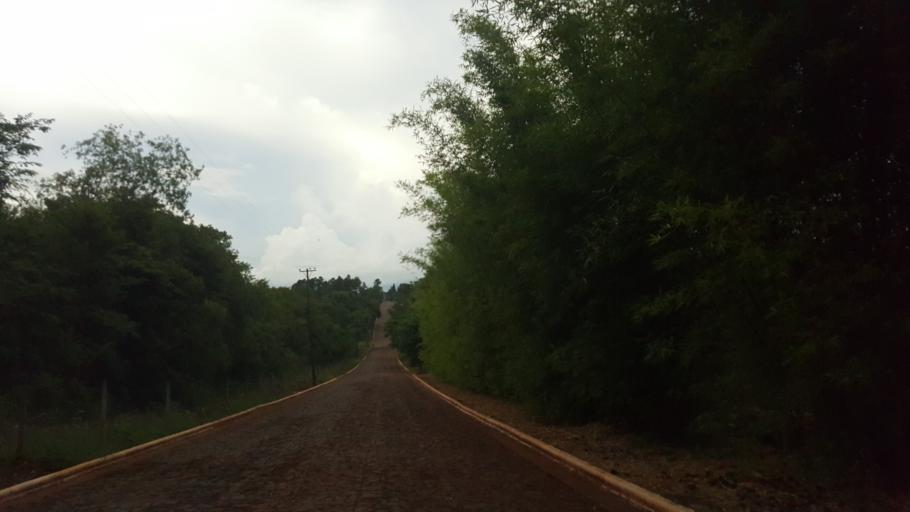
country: AR
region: Misiones
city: Jardin America
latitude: -27.0788
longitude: -55.2864
